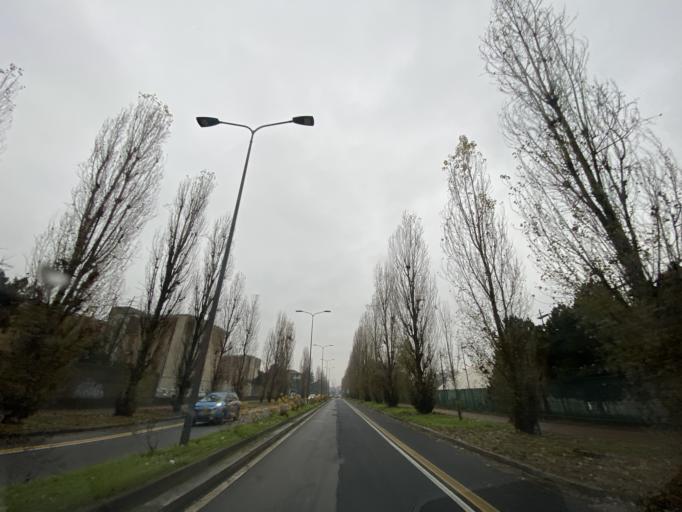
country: IT
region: Lombardy
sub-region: Citta metropolitana di Milano
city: Cesano Boscone
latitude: 45.4674
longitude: 9.1121
